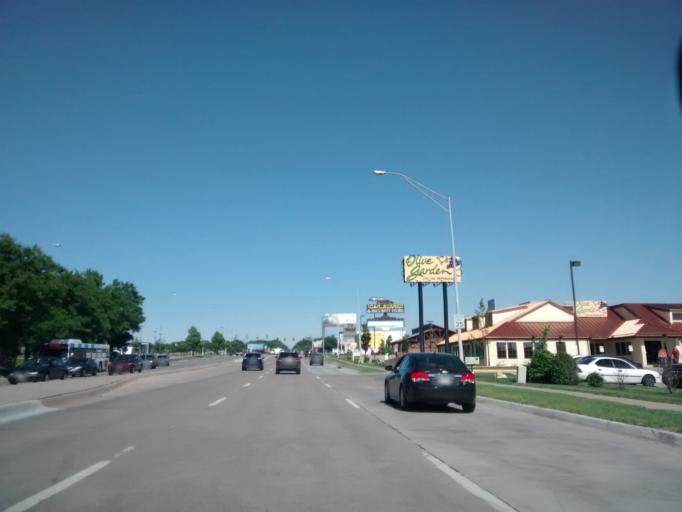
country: US
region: Nebraska
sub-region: Douglas County
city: Ralston
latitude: 41.2596
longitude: -96.0298
